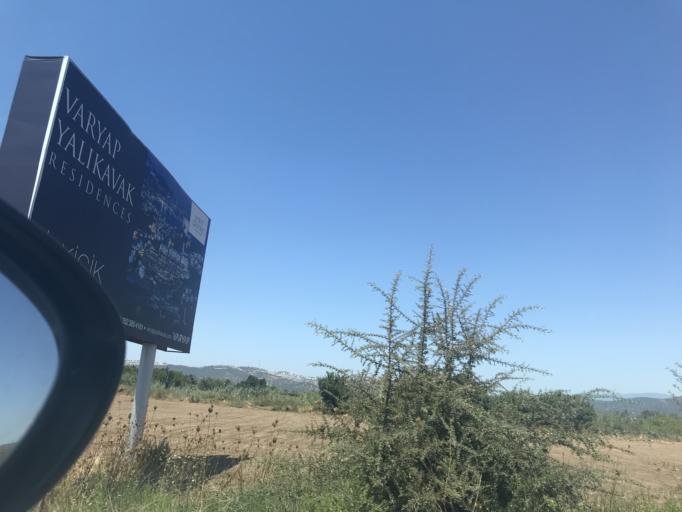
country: TR
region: Mugla
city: Kiulukioi
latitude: 37.1725
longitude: 27.6002
